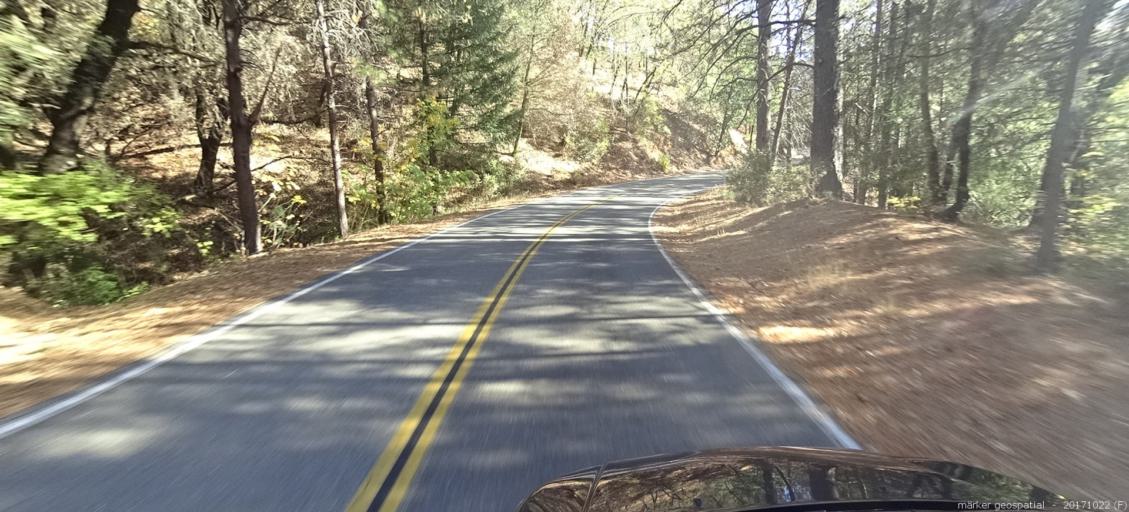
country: US
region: California
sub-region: Shasta County
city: Shasta Lake
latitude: 40.8751
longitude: -122.2460
